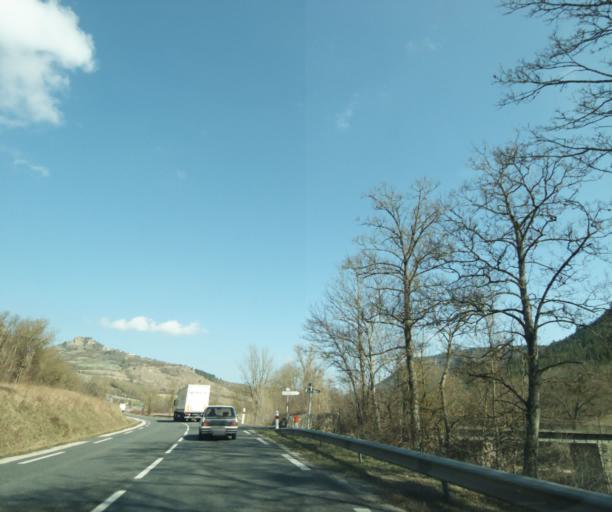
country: FR
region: Languedoc-Roussillon
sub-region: Departement de la Lozere
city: Chanac
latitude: 44.4946
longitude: 3.3958
